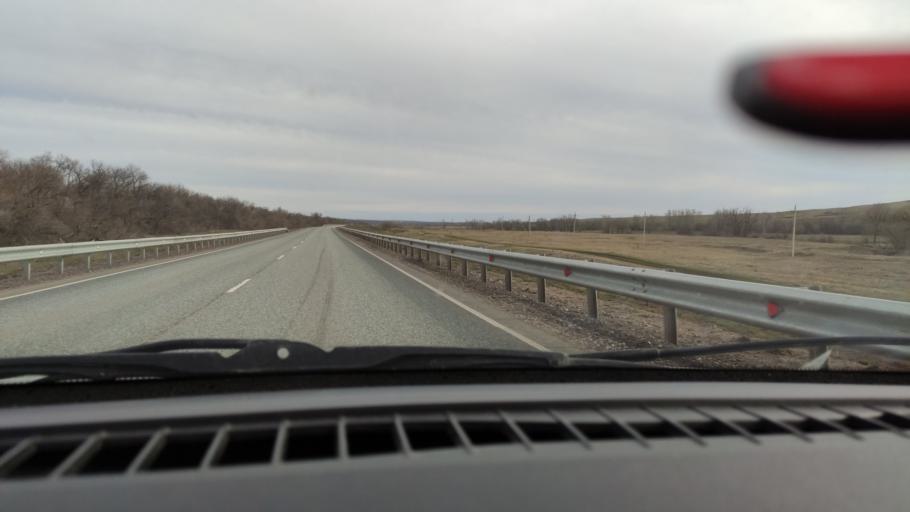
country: RU
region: Bashkortostan
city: Yermolayevo
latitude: 52.6145
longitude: 55.8453
